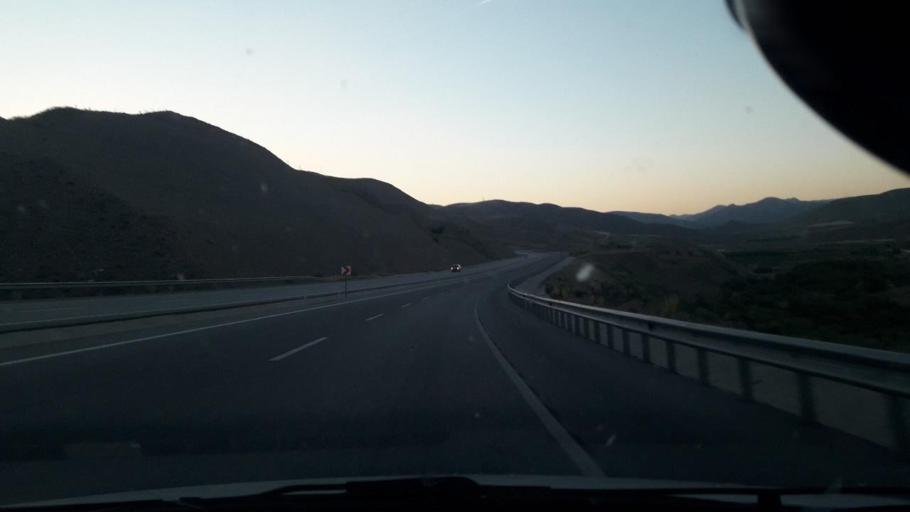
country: TR
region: Malatya
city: Yazihan
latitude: 38.6241
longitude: 38.1657
